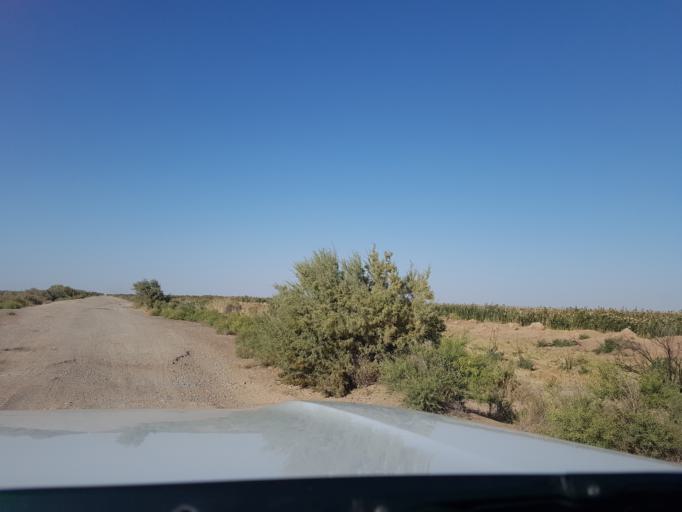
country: IR
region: Razavi Khorasan
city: Sarakhs
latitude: 36.9447
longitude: 61.3787
